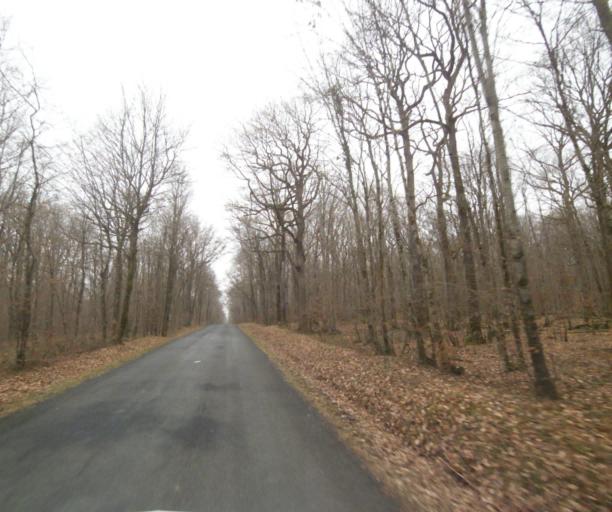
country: FR
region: Champagne-Ardenne
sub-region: Departement de la Haute-Marne
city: Bienville
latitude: 48.5531
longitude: 5.0011
